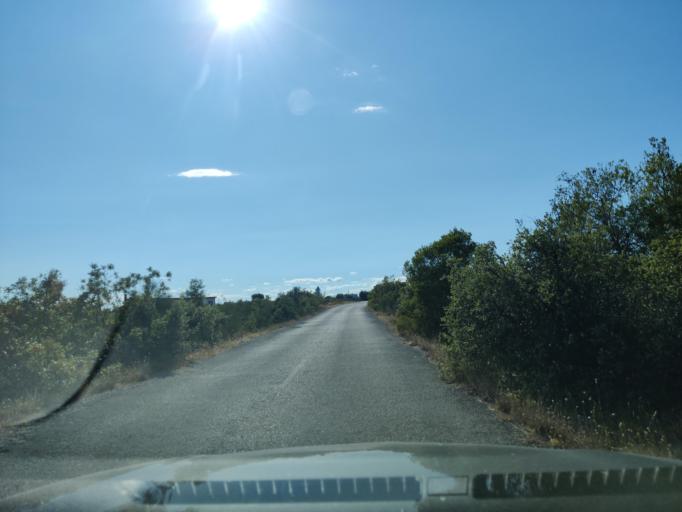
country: HR
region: Sibensko-Kniniska
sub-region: Grad Sibenik
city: Sibenik
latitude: 43.7401
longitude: 15.8607
